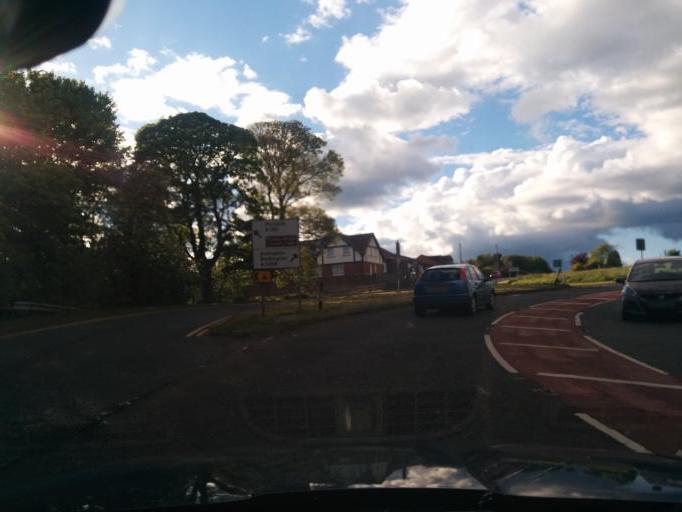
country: GB
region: England
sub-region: Northumberland
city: Bedlington
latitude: 55.1142
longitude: -1.6232
